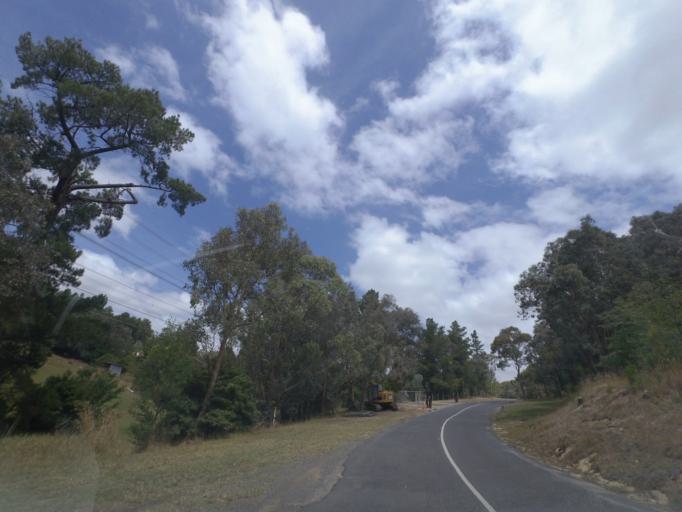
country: AU
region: Victoria
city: Mitcham
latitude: -37.7990
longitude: 145.2125
